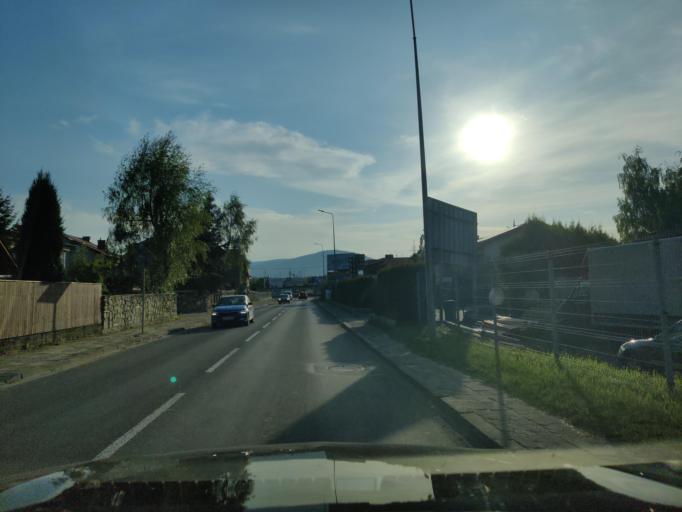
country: PL
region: Silesian Voivodeship
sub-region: Powiat zywiecki
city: Zywiec
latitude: 49.6917
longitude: 19.1959
